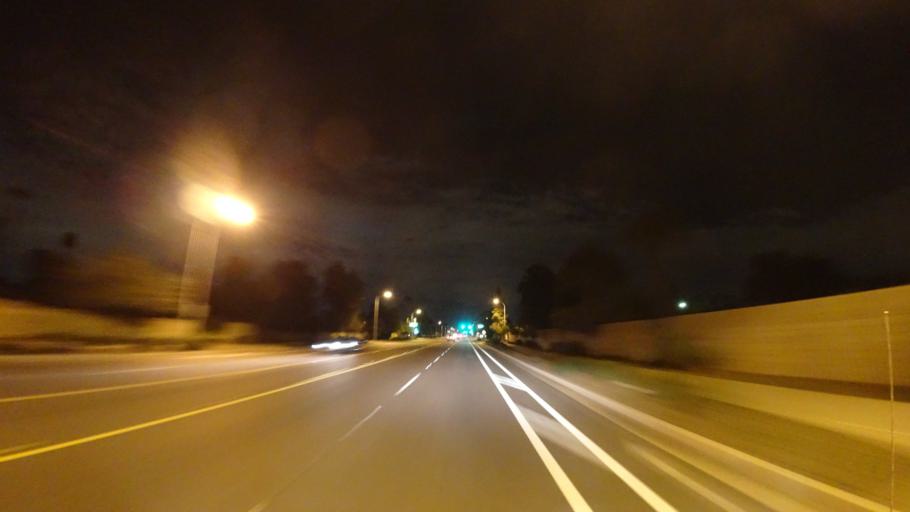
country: US
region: Arizona
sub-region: Maricopa County
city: Tempe
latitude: 33.3679
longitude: -111.9112
